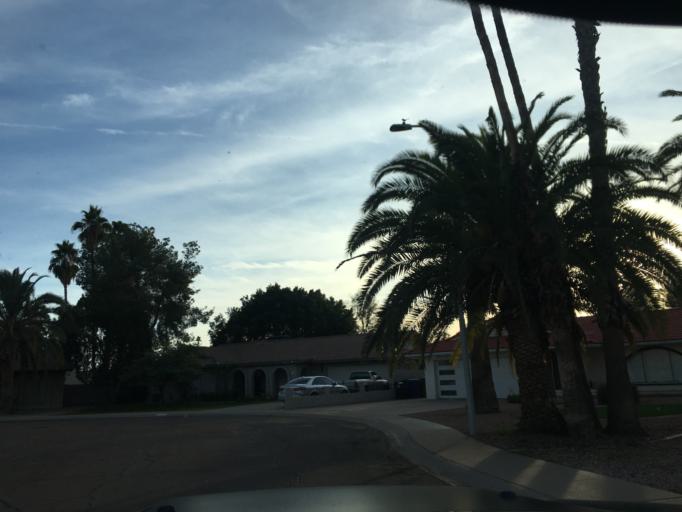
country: US
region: Arizona
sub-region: Maricopa County
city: Tempe
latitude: 33.3743
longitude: -111.9106
